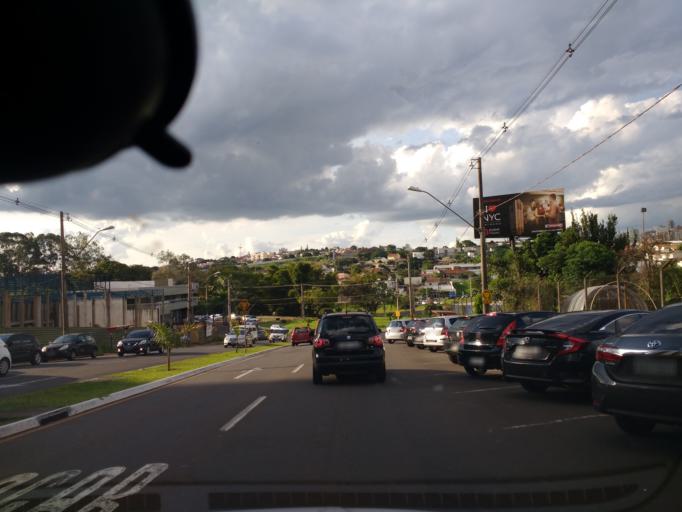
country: BR
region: Parana
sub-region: Londrina
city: Londrina
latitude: -23.3271
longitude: -51.1772
